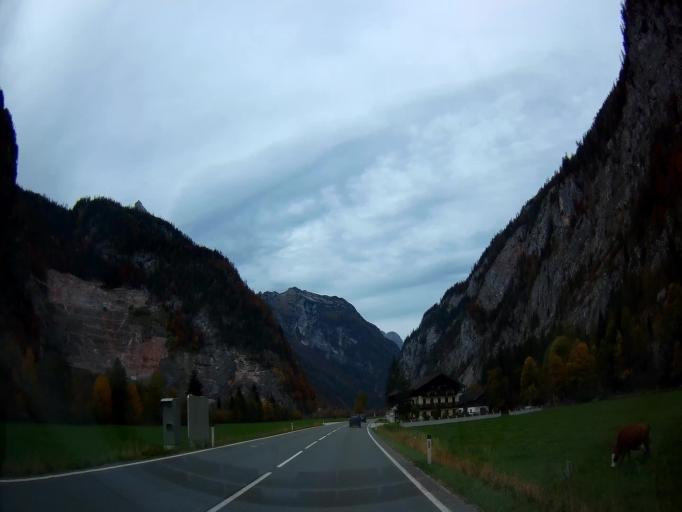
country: AT
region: Salzburg
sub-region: Politischer Bezirk Zell am See
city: Leogang
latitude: 47.4974
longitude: 12.7967
